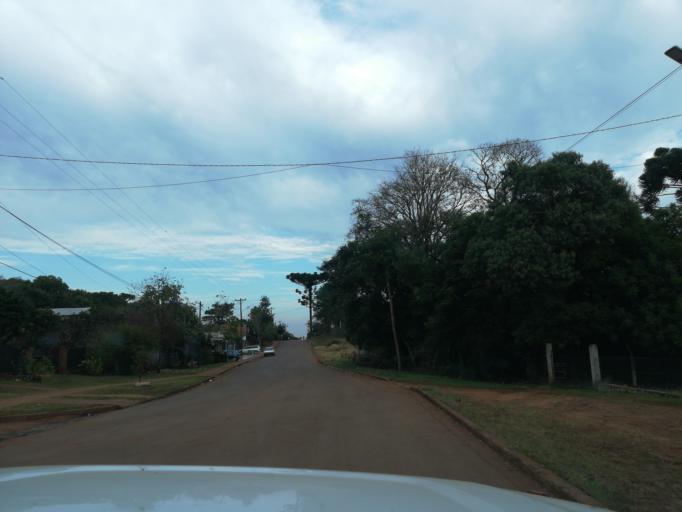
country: AR
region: Misiones
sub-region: Departamento de San Pedro
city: San Pedro
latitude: -26.6245
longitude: -54.0991
